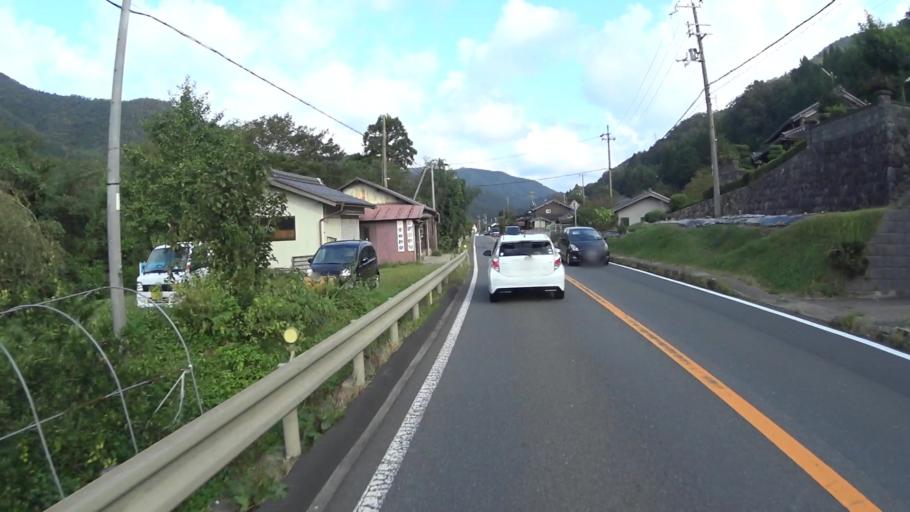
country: JP
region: Kyoto
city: Ayabe
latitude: 35.2293
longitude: 135.4155
